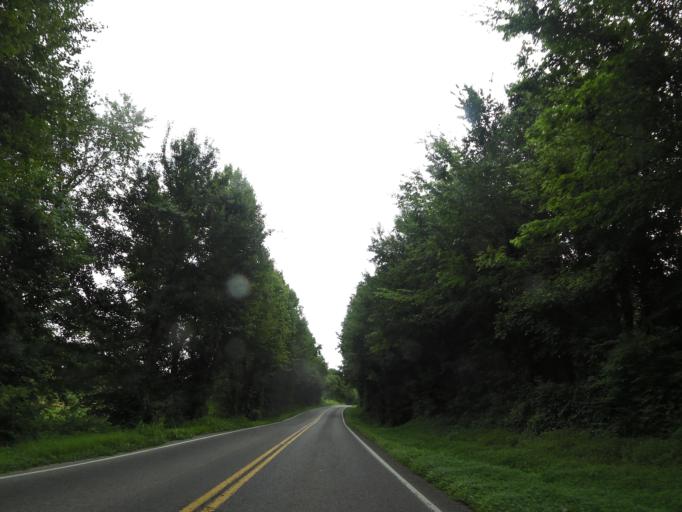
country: US
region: Kentucky
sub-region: Ballard County
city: Wickliffe
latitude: 36.9766
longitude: -89.0426
